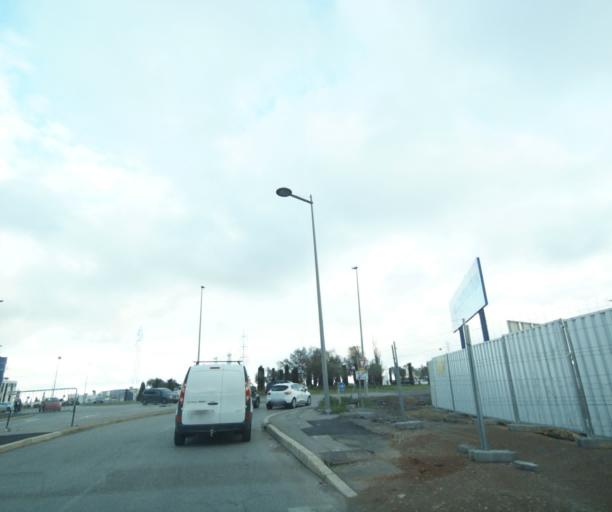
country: FR
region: Languedoc-Roussillon
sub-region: Departement de l'Herault
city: Saint-Jean-de-Vedas
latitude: 43.5707
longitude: 3.8371
